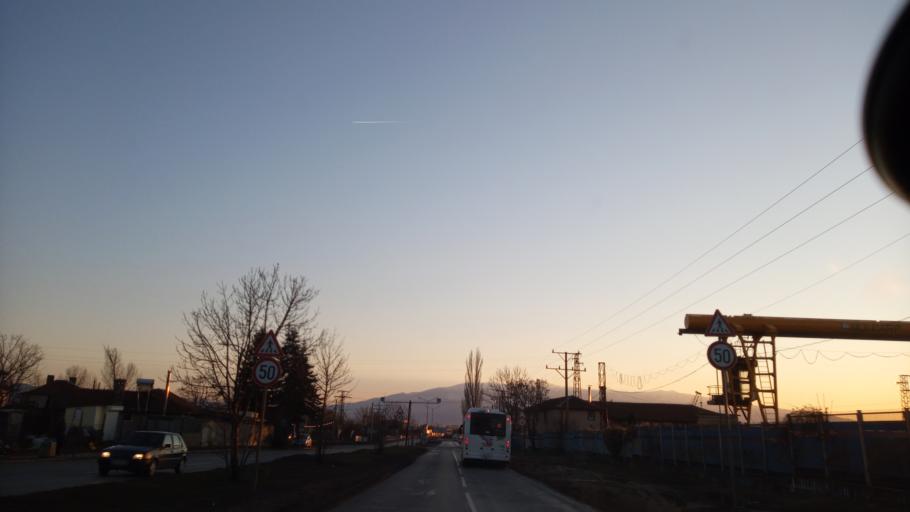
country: BG
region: Sofia-Capital
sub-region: Stolichna Obshtina
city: Bukhovo
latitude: 42.7338
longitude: 23.4661
